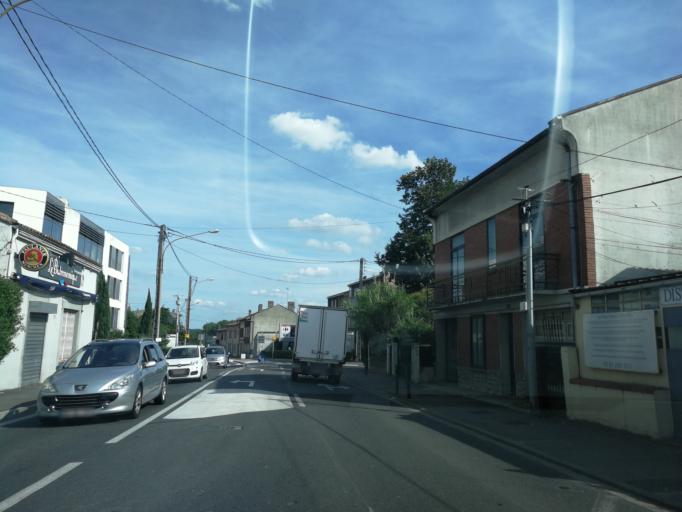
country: FR
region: Midi-Pyrenees
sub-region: Departement de la Haute-Garonne
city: Ramonville-Saint-Agne
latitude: 43.5742
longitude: 1.4908
